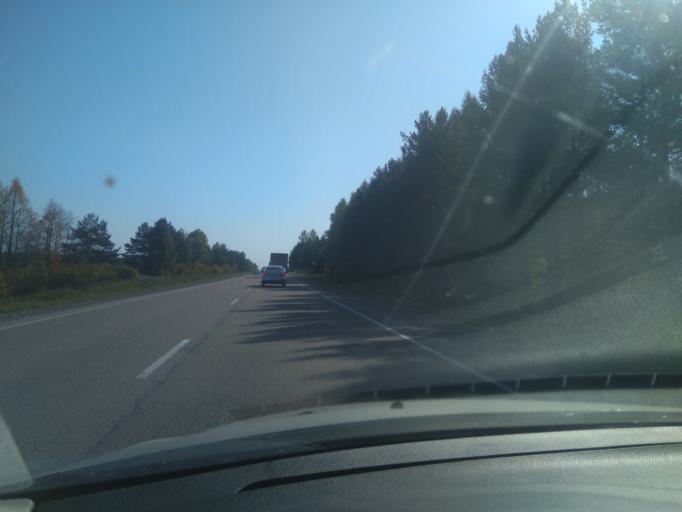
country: RU
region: Sverdlovsk
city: Dvurechensk
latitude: 56.6828
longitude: 61.1216
